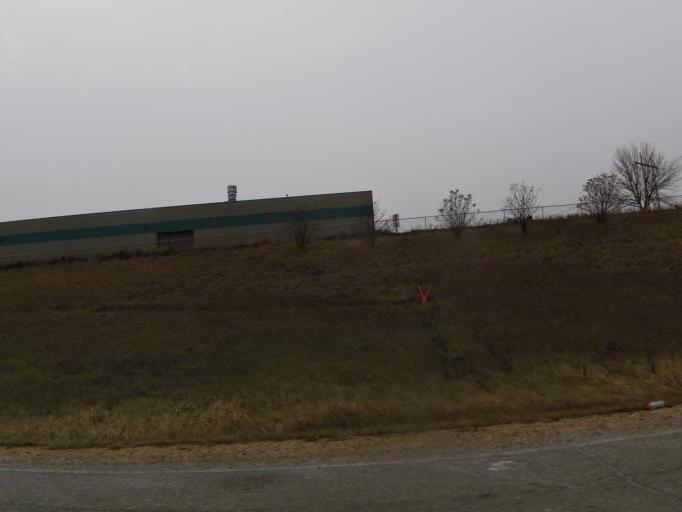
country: US
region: Minnesota
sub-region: Washington County
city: Oakdale
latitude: 44.9541
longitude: -92.9588
